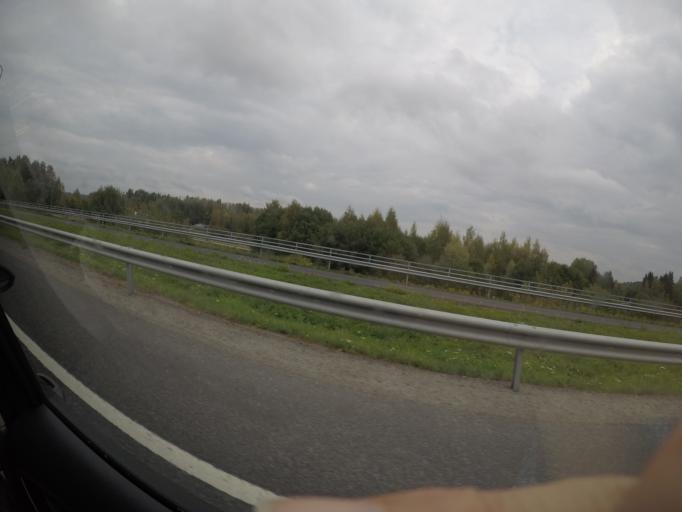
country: FI
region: Haeme
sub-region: Haemeenlinna
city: Haemeenlinna
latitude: 61.0228
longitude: 24.4222
